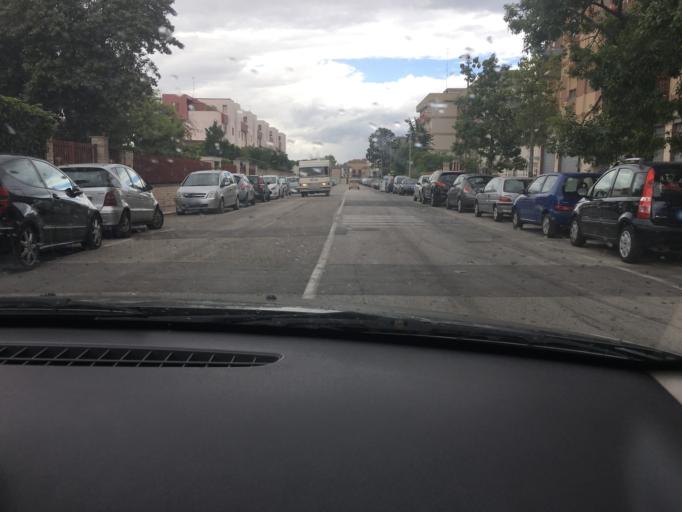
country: IT
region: Apulia
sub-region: Provincia di Bari
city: San Paolo
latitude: 41.1340
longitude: 16.8260
